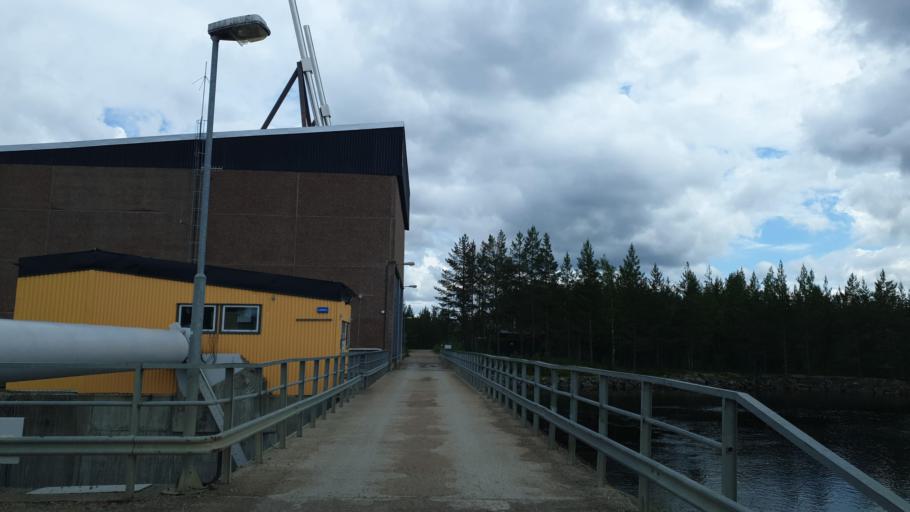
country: SE
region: Jaemtland
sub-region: Harjedalens Kommun
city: Sveg
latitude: 62.0420
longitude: 14.4955
